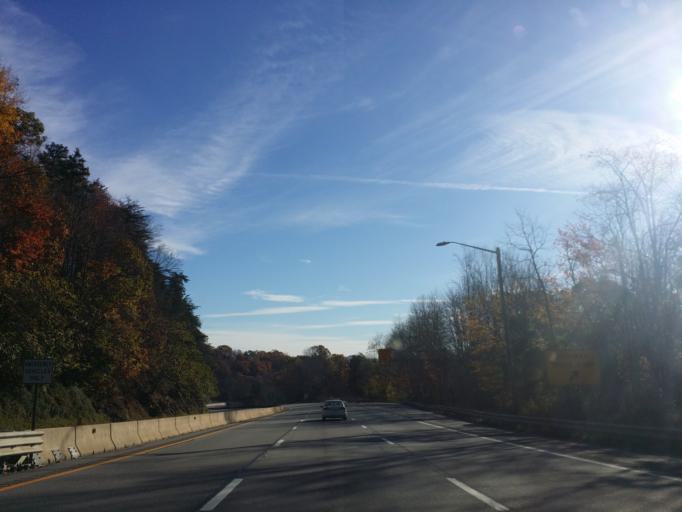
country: US
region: North Carolina
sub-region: Buncombe County
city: Black Mountain
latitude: 35.6247
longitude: -82.2106
